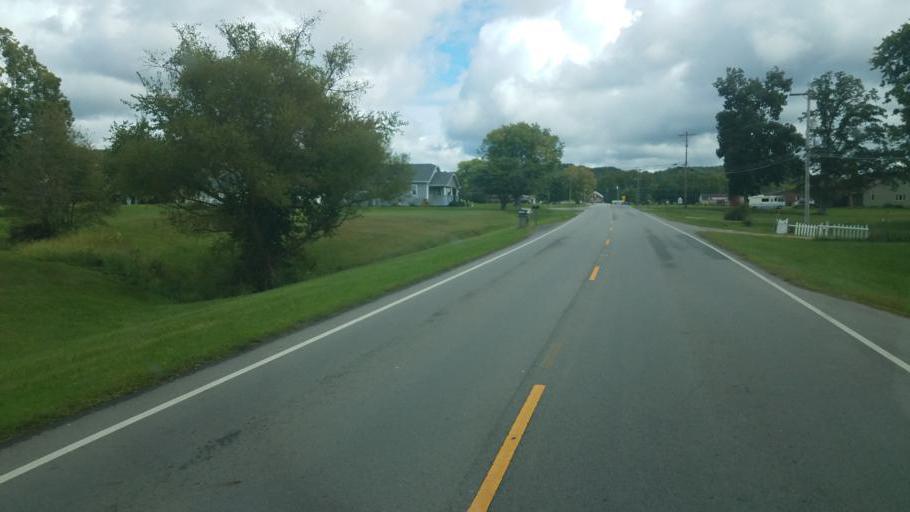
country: US
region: Ohio
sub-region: Scioto County
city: Sciotodale
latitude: 38.8661
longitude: -82.8438
